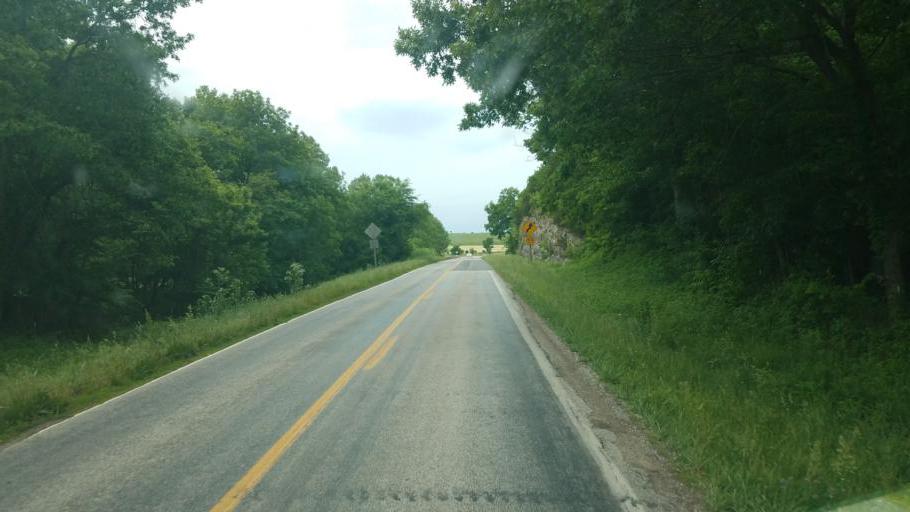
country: US
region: Missouri
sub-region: Moniteau County
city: California
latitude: 38.6883
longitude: -92.6139
